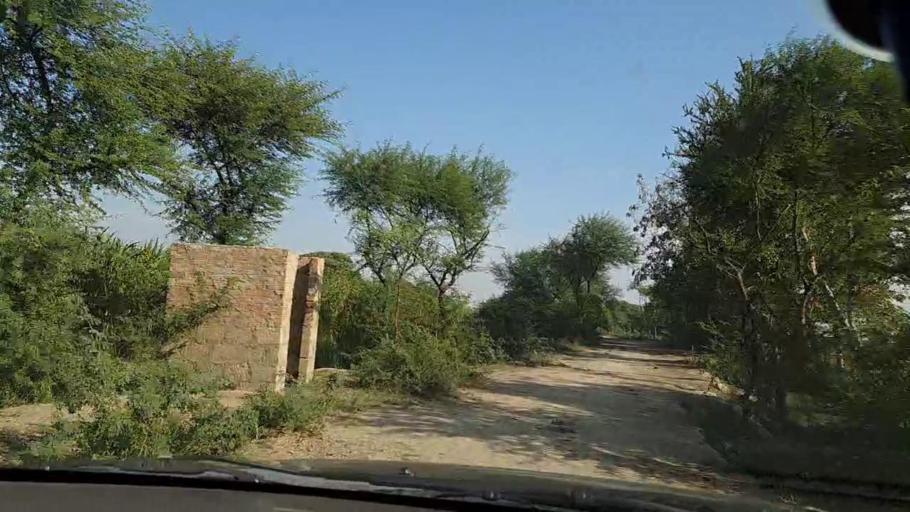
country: PK
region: Sindh
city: Mirpur Batoro
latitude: 24.6121
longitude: 68.2689
